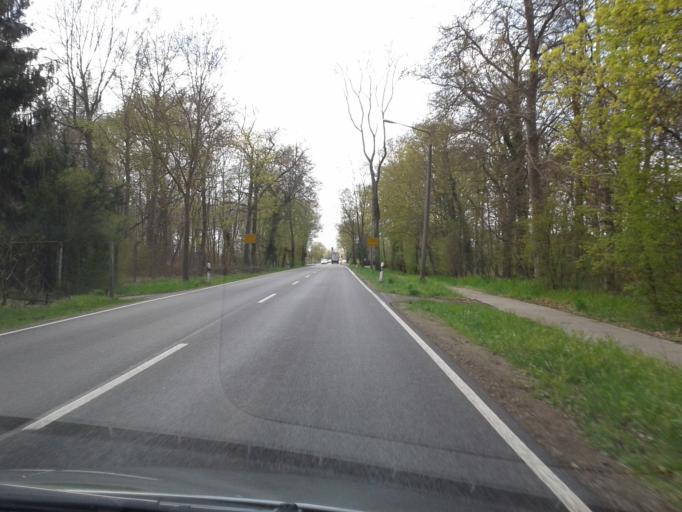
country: DE
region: Lower Saxony
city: Lubbow
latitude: 52.8898
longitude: 11.1768
